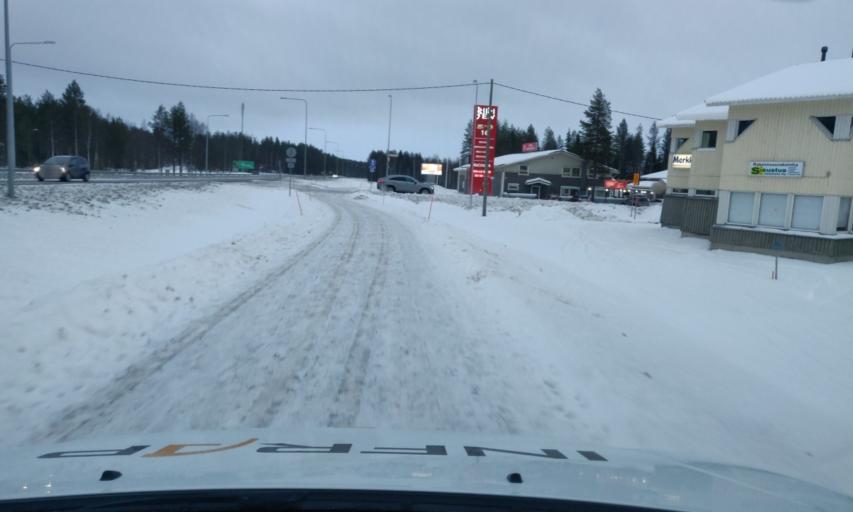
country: FI
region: Northern Ostrobothnia
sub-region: Koillismaa
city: Kuusamo
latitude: 65.9903
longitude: 29.1556
